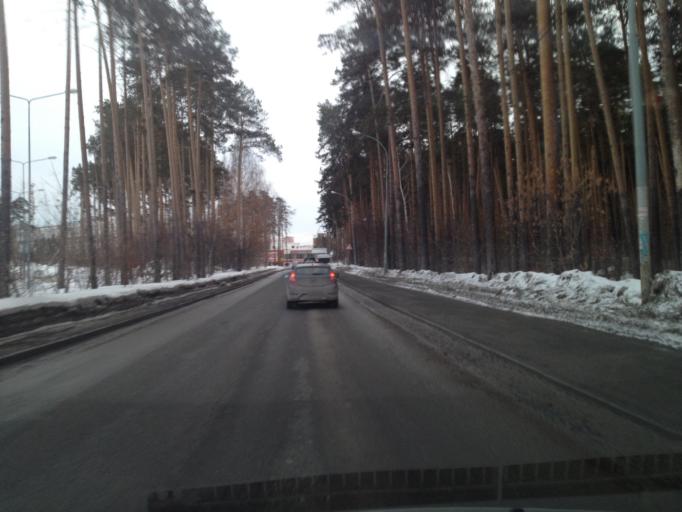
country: RU
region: Sverdlovsk
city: Shirokaya Rechka
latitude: 56.8160
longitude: 60.5342
